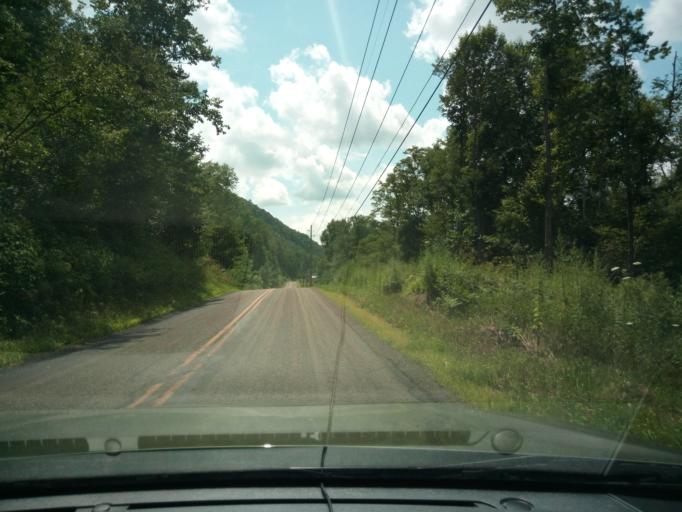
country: US
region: Pennsylvania
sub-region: Bradford County
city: South Waverly
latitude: 41.9927
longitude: -76.6020
